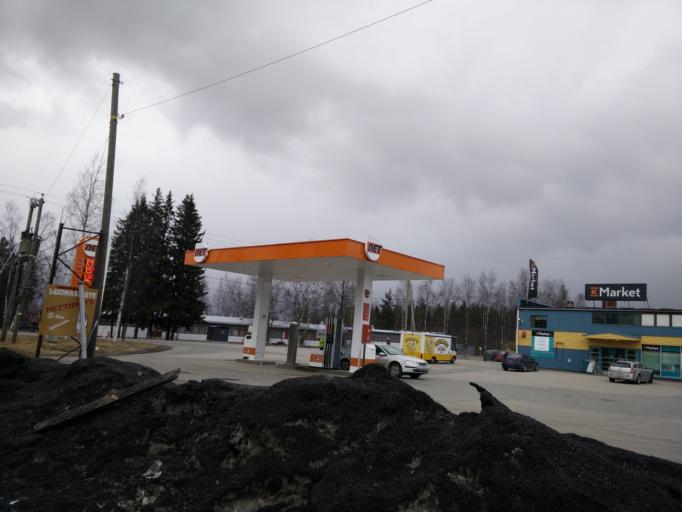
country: FI
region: Pirkanmaa
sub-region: Tampere
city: Orivesi
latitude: 61.6923
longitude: 24.3551
